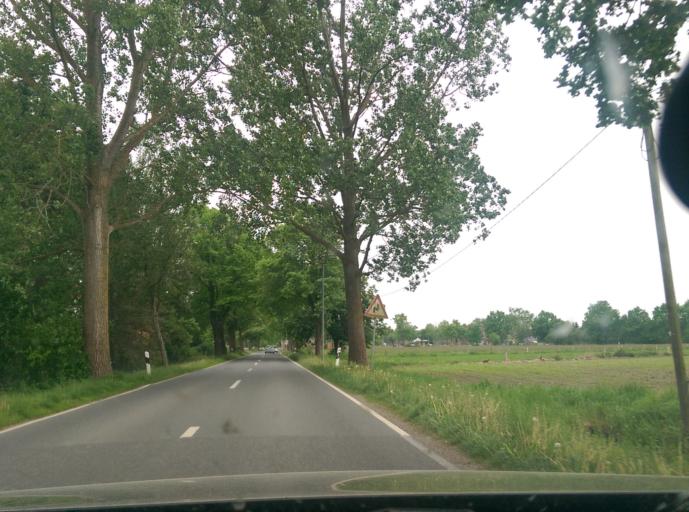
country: DE
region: Lower Saxony
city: Garbsen-Mitte
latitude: 52.4736
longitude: 9.6218
